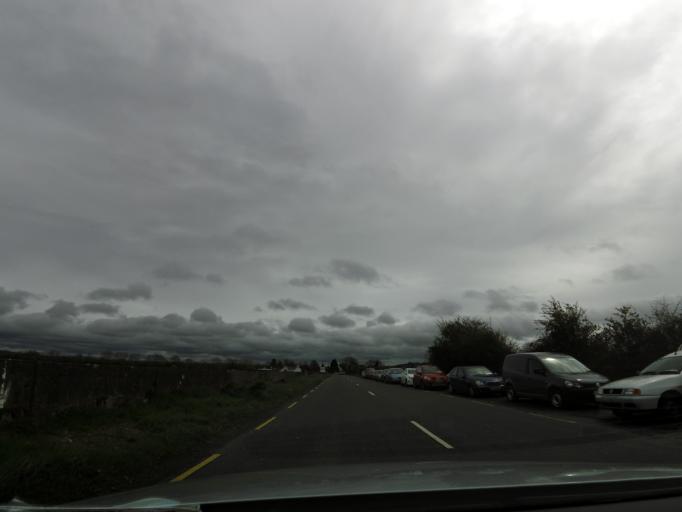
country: IE
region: Leinster
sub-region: Kilkenny
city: Ballyragget
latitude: 52.7357
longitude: -7.4135
